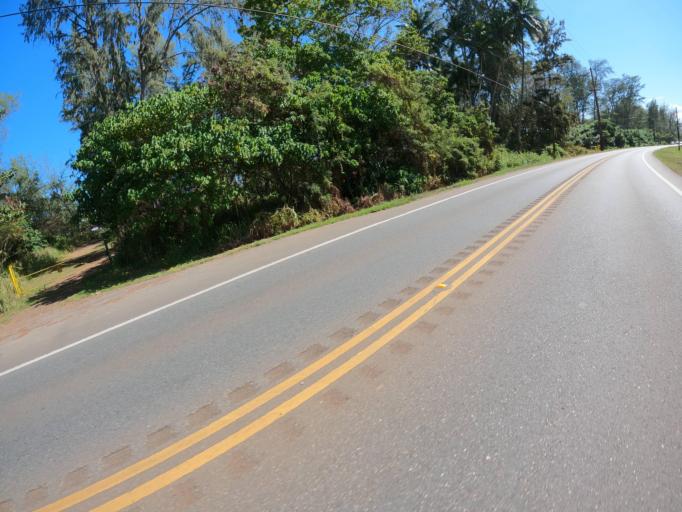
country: US
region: Hawaii
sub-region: Honolulu County
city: Kahuku
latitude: 21.6712
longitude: -157.9396
